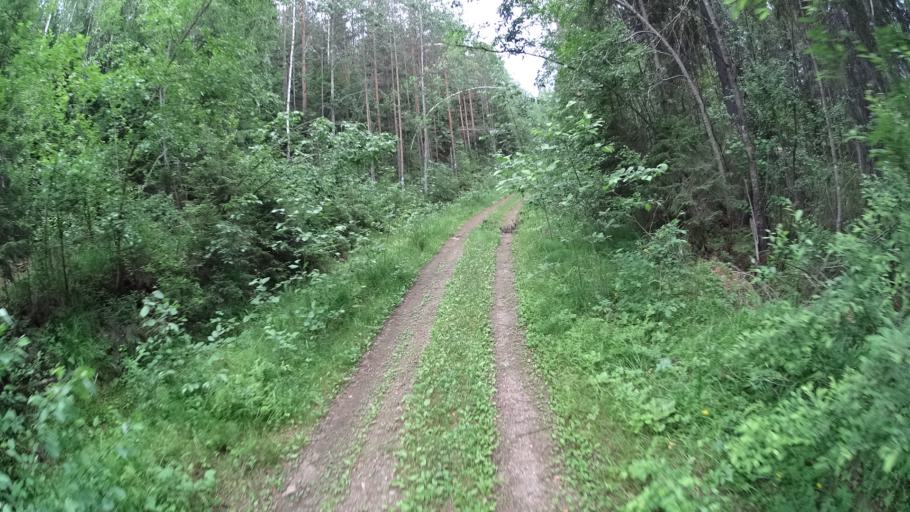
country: FI
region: Southern Savonia
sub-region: Mikkeli
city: Maentyharju
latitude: 61.1749
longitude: 26.8969
